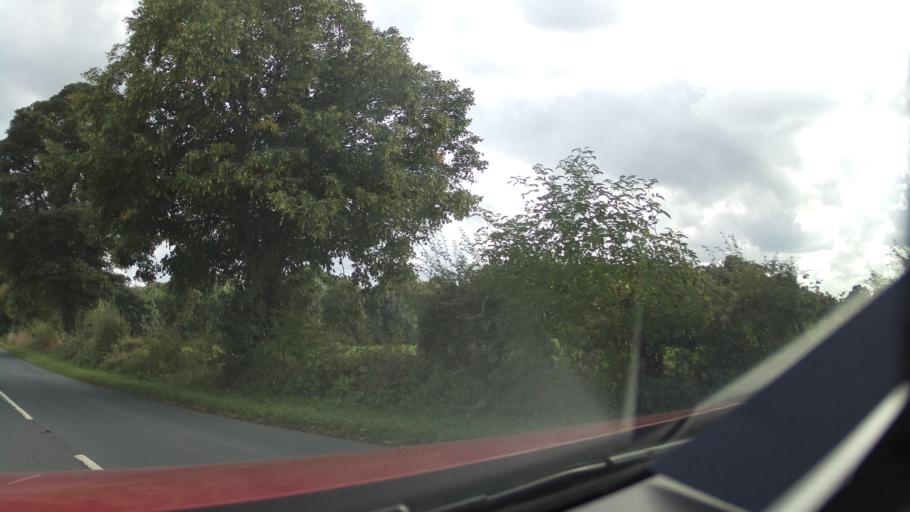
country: GB
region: England
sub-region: North Yorkshire
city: Bedale
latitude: 54.2025
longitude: -1.5851
